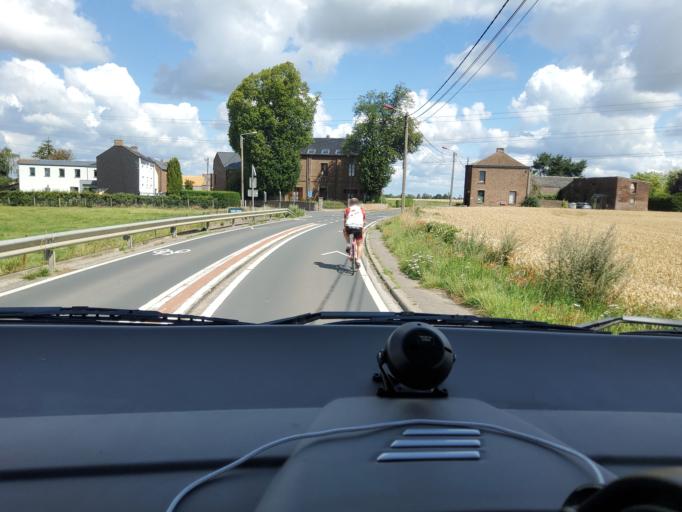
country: BE
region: Wallonia
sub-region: Province du Hainaut
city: Fleurus
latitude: 50.4929
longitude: 4.5495
